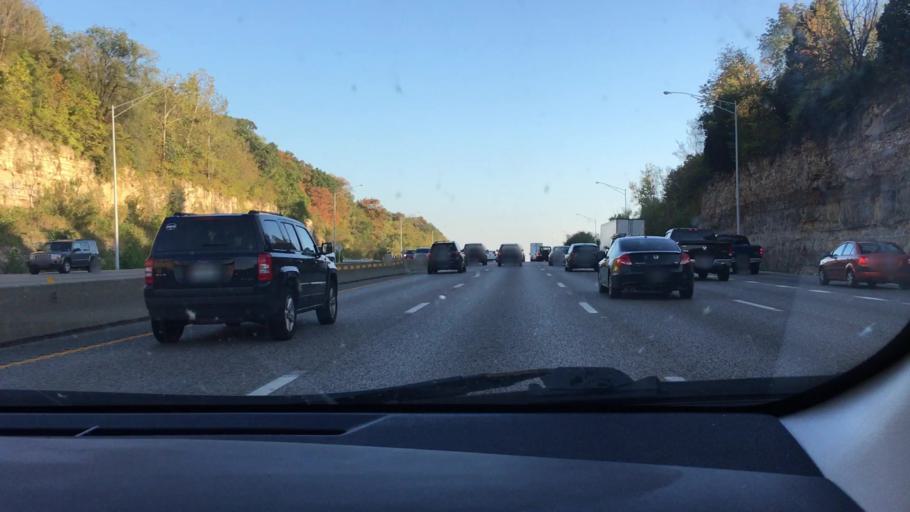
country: US
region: Missouri
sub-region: Saint Louis County
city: Sunset Hills
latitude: 38.5578
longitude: -90.4356
